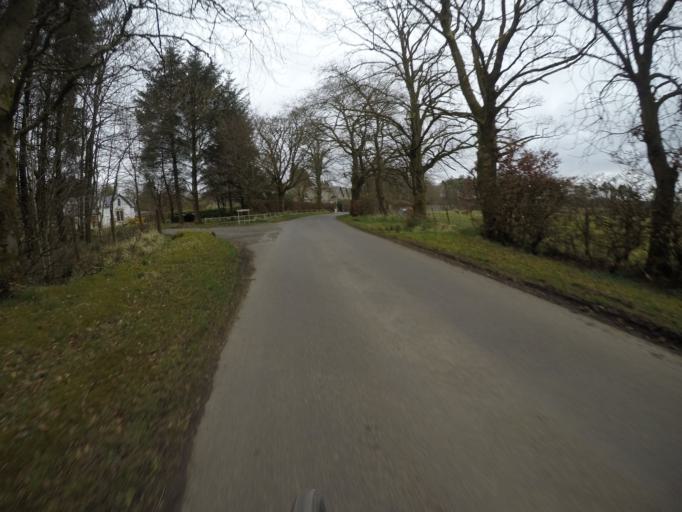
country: GB
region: Scotland
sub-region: East Ayrshire
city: Galston
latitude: 55.6629
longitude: -4.3770
